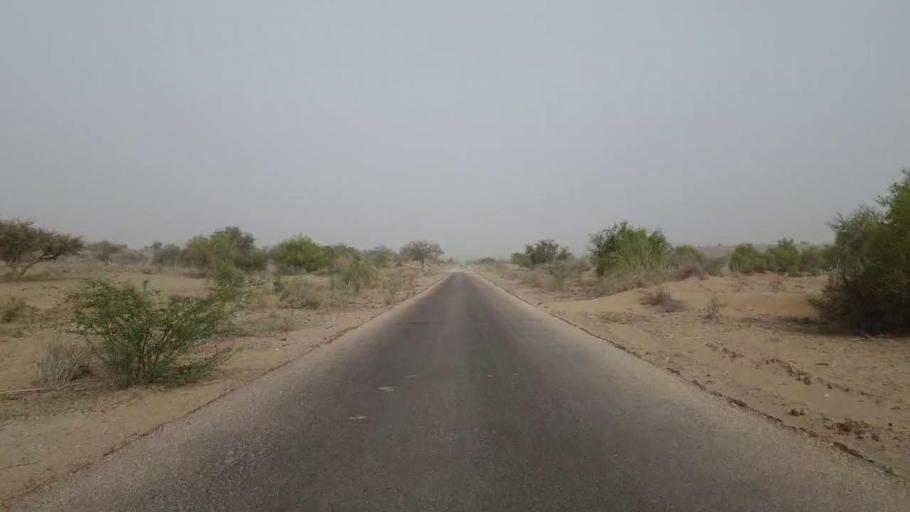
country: PK
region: Sindh
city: Islamkot
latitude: 24.5820
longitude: 70.3008
